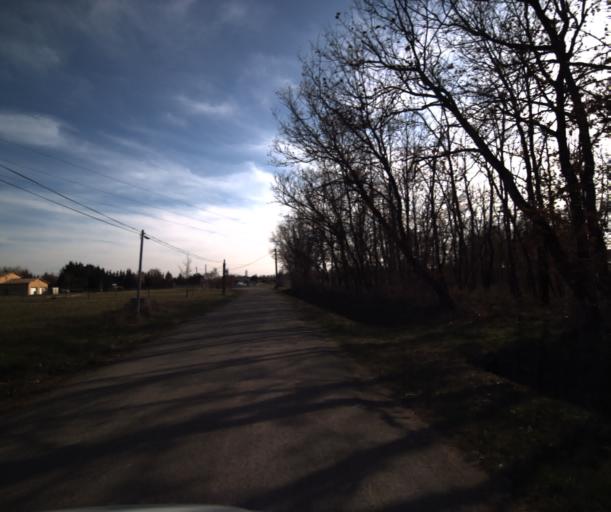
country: FR
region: Midi-Pyrenees
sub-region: Departement du Tarn-et-Garonne
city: Campsas
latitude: 43.9156
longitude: 1.3278
